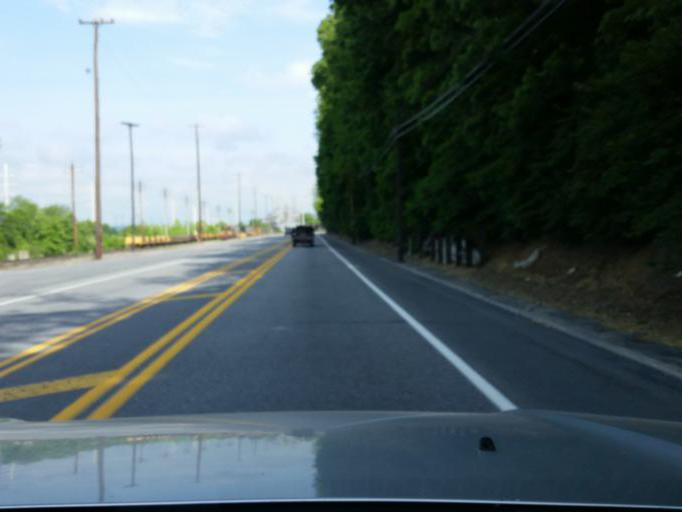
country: US
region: Pennsylvania
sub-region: Dauphin County
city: Bressler
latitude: 40.2186
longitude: -76.8196
